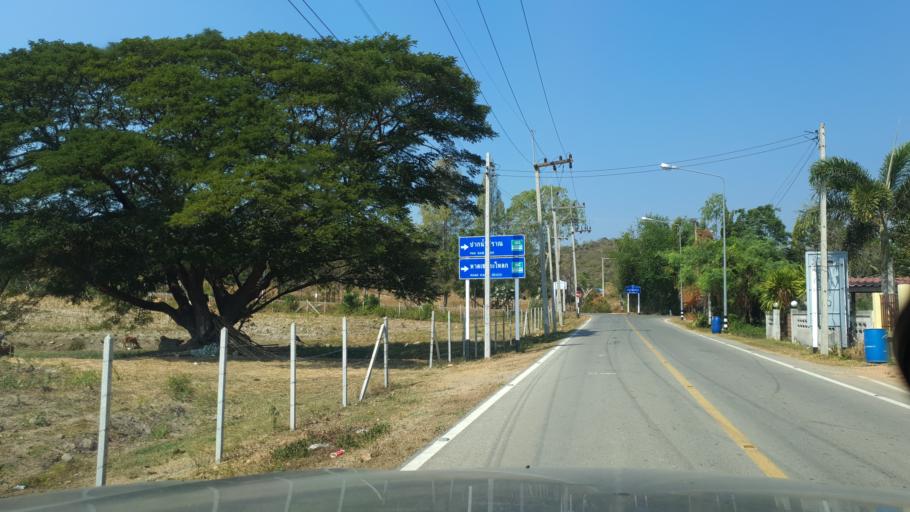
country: TH
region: Prachuap Khiri Khan
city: Sam Roi Yot
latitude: 12.2852
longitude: 99.9716
